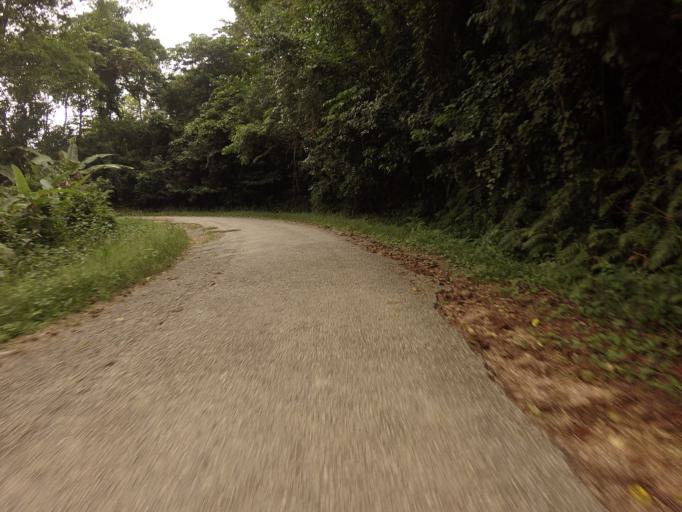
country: GH
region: Volta
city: Kpandu
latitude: 6.8346
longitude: 0.4266
